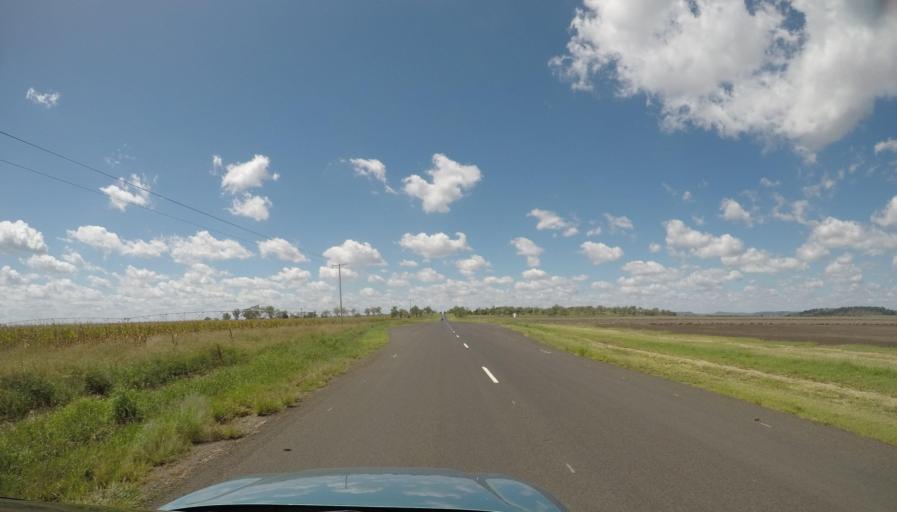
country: AU
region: Queensland
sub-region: Toowoomba
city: Oakey
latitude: -27.5274
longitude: 151.5798
